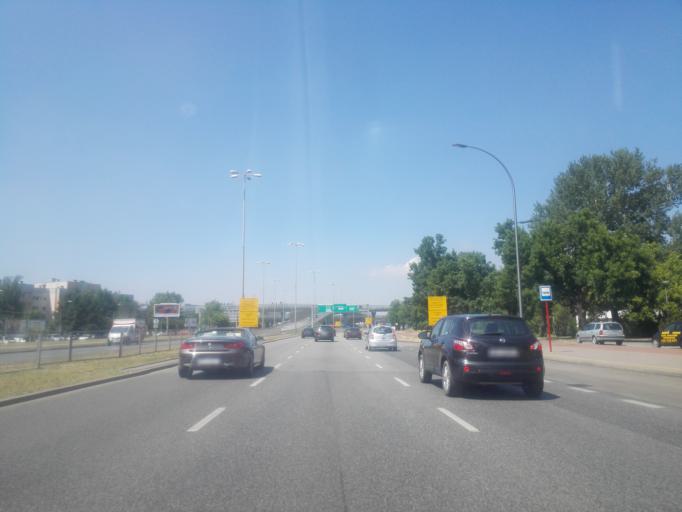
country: PL
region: Masovian Voivodeship
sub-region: Warszawa
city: Mokotow
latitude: 52.1945
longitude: 21.0548
